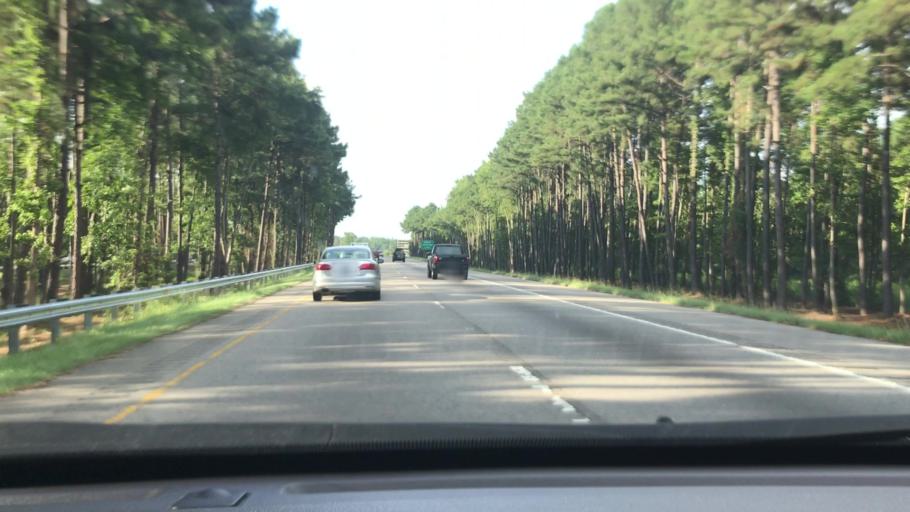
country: US
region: North Carolina
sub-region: Robeson County
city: Lumberton
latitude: 34.6885
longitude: -78.9997
